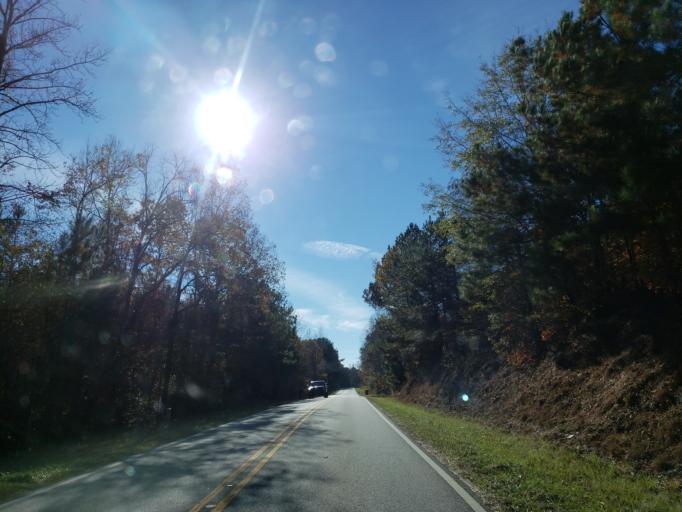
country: US
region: Alabama
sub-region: Cleburne County
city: Heflin
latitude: 33.6026
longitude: -85.6125
